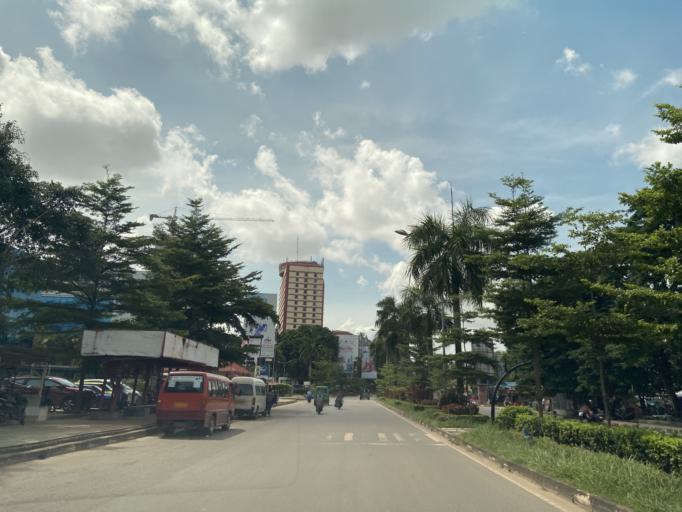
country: SG
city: Singapore
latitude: 1.1522
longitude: 104.0048
